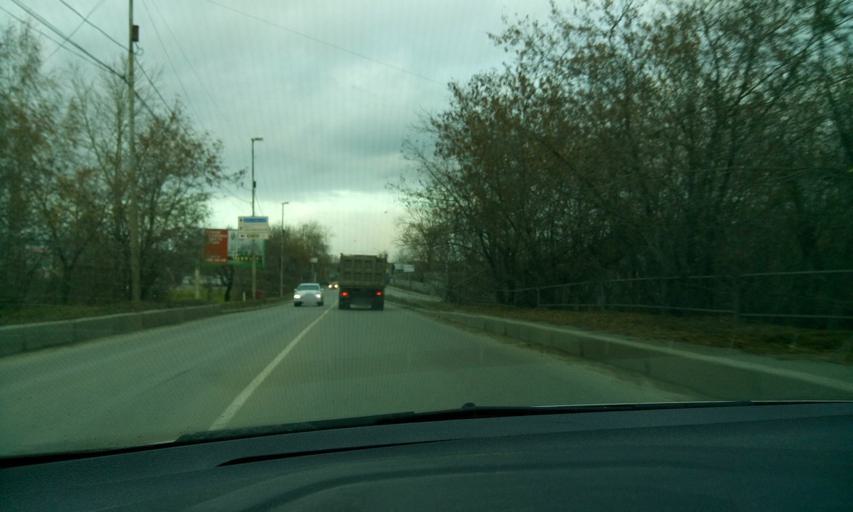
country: RU
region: Sverdlovsk
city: Yekaterinburg
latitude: 56.8685
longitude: 60.6771
